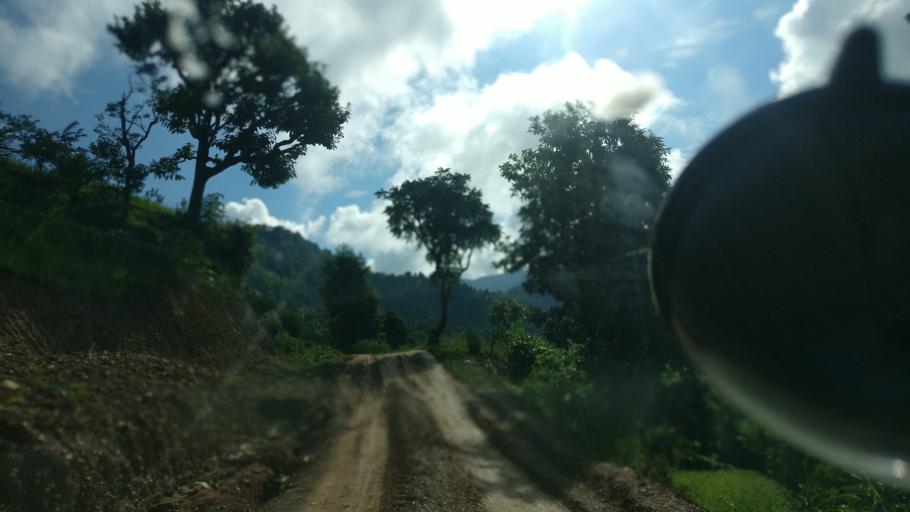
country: NP
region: Western Region
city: Baglung
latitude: 28.1368
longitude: 83.6473
